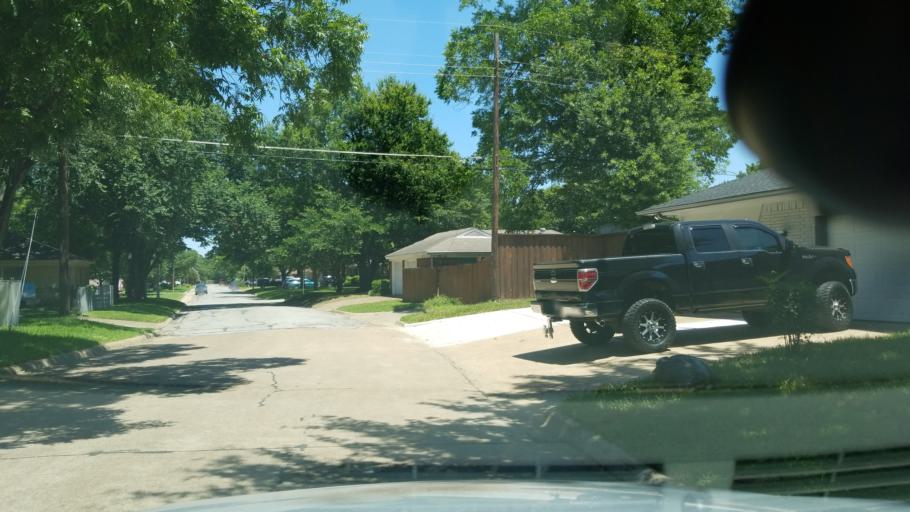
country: US
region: Texas
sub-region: Dallas County
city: Irving
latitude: 32.8265
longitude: -96.9314
